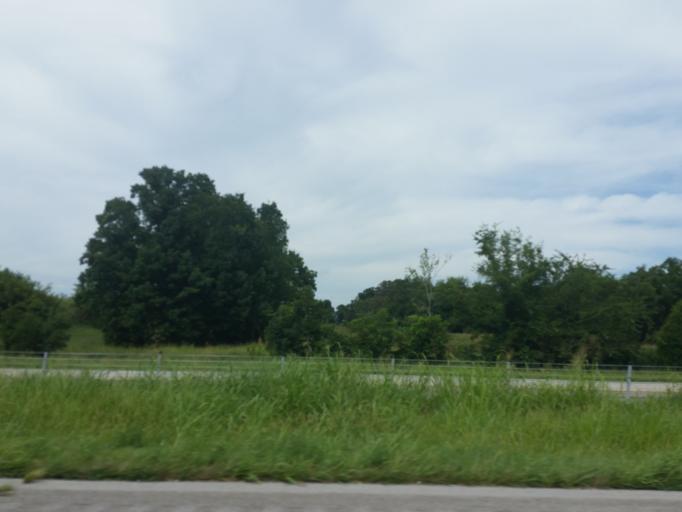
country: US
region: Kentucky
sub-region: Trigg County
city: Cadiz
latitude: 36.9105
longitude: -87.7808
